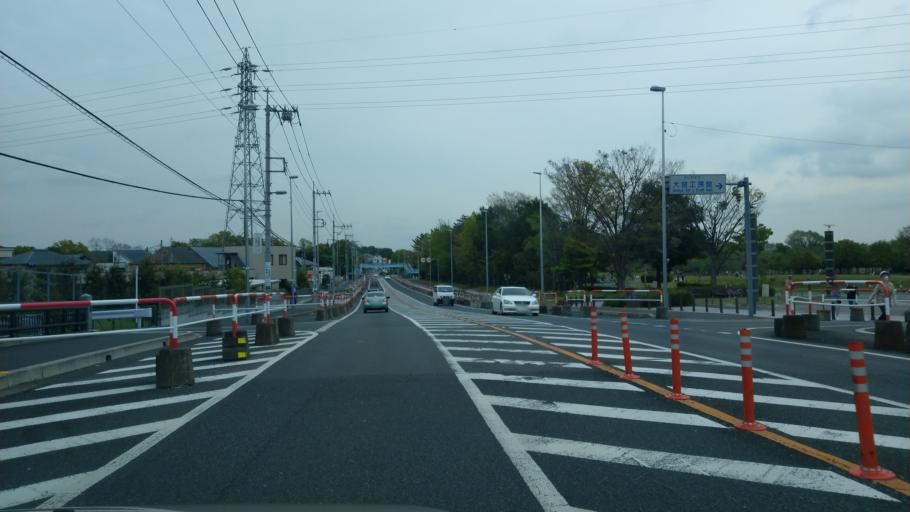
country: JP
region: Saitama
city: Saitama
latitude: 35.9144
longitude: 139.6392
